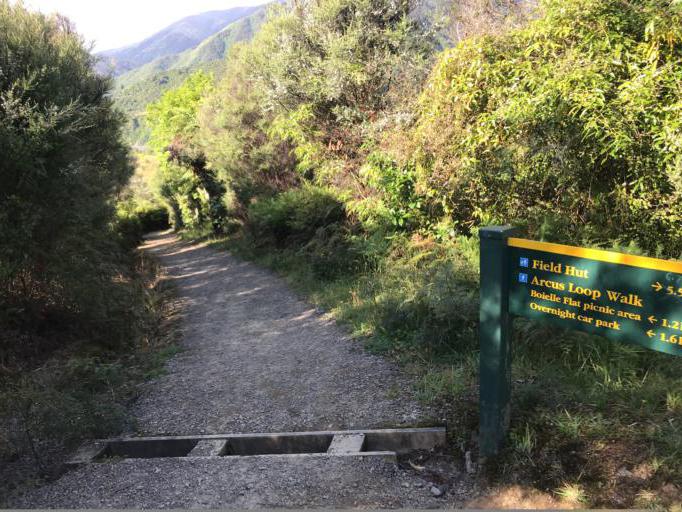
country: NZ
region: Wellington
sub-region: Kapiti Coast District
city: Otaki
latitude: -40.8761
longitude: 175.2346
